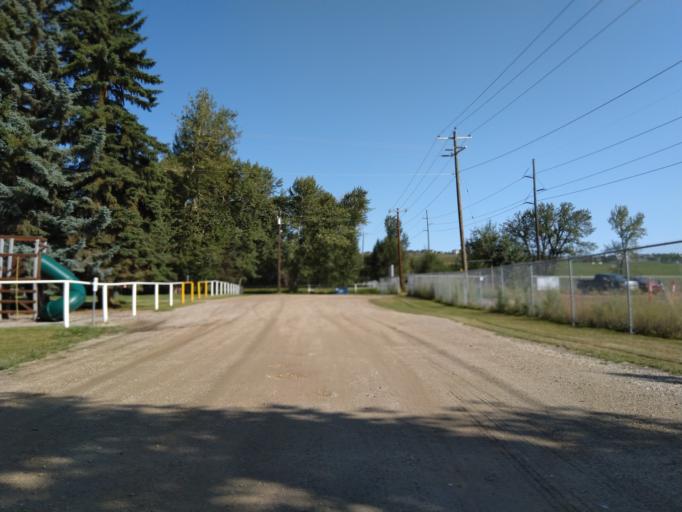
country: CA
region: Alberta
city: Calgary
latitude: 51.0990
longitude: -114.2345
